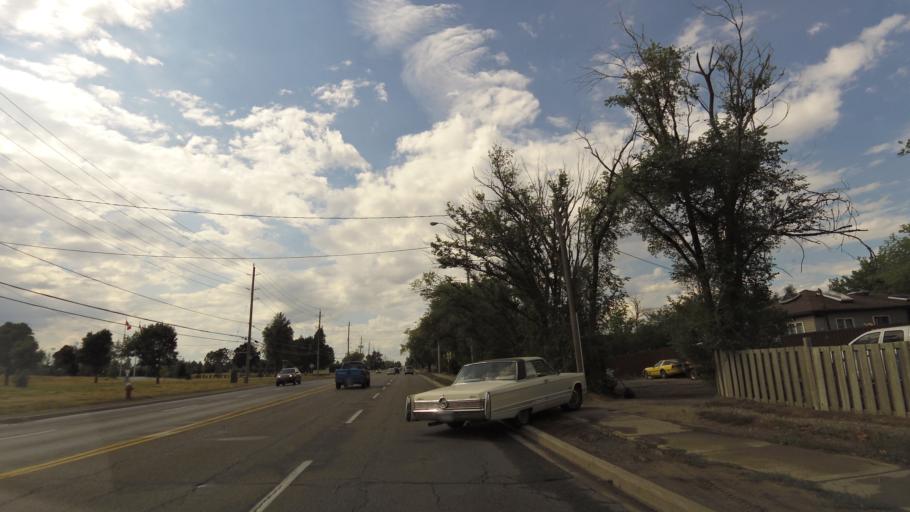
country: CA
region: Ontario
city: Brampton
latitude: 43.6704
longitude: -79.7627
